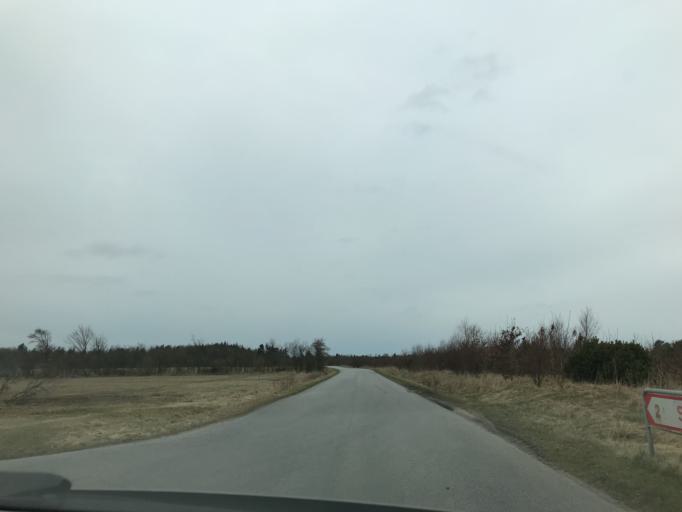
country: DK
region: South Denmark
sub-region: Varde Kommune
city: Oksbol
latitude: 55.8041
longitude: 8.3345
